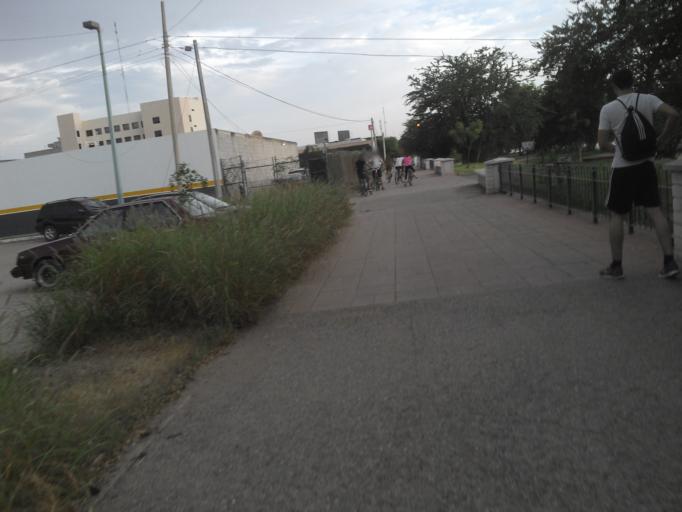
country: MX
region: Sinaloa
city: Culiacan
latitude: 24.8213
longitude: -107.4017
